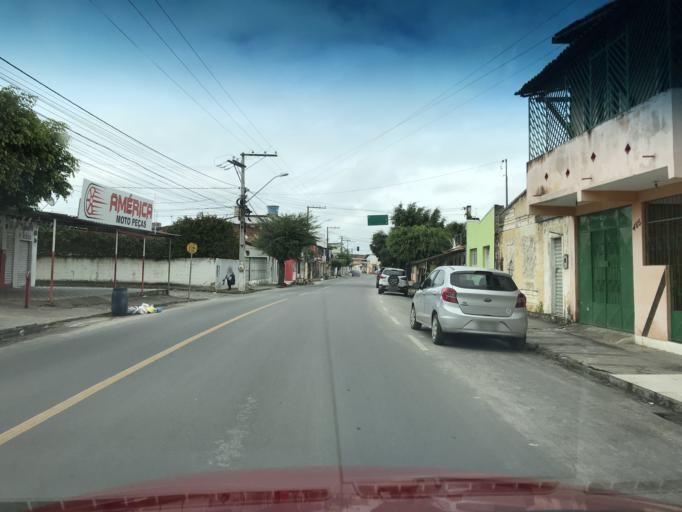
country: BR
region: Bahia
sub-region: Cruz Das Almas
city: Cruz das Almas
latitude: -12.6660
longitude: -39.0999
